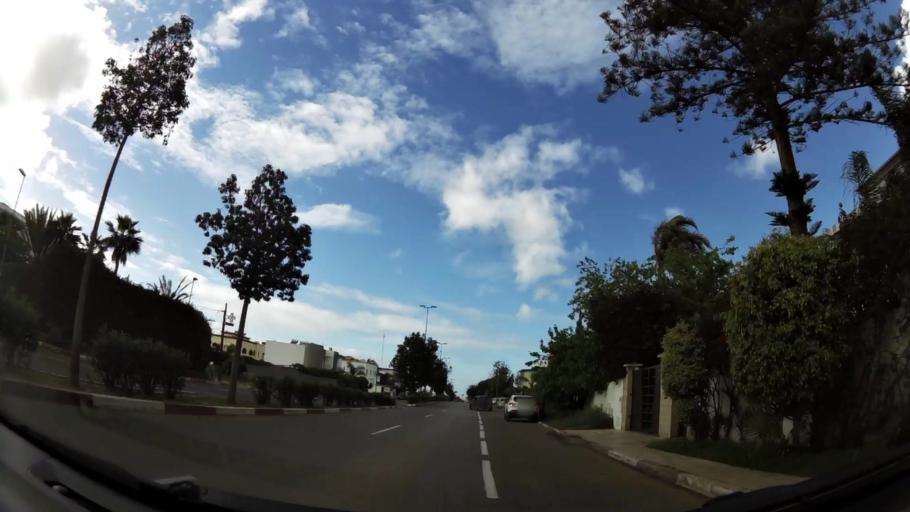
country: MA
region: Grand Casablanca
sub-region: Casablanca
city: Casablanca
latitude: 33.5461
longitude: -7.6214
